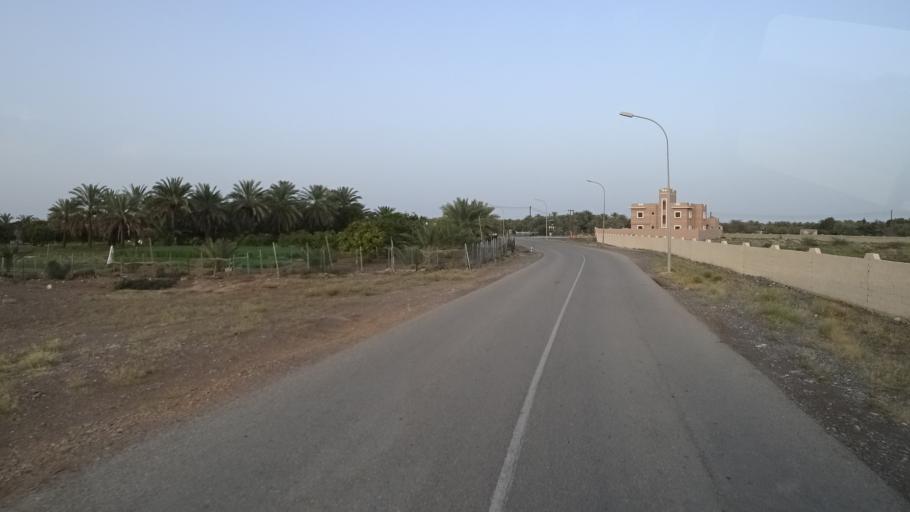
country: OM
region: Muhafazat Masqat
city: Muscat
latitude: 23.2069
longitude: 58.9687
